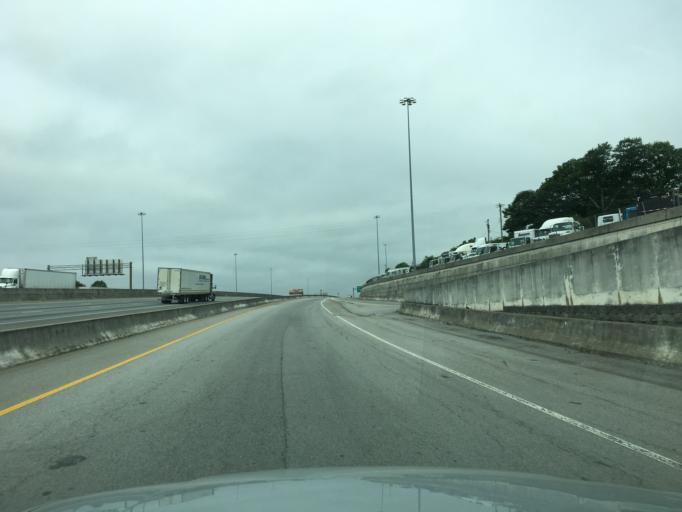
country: US
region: South Carolina
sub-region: Greenville County
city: Gantt
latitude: 34.7876
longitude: -82.4215
